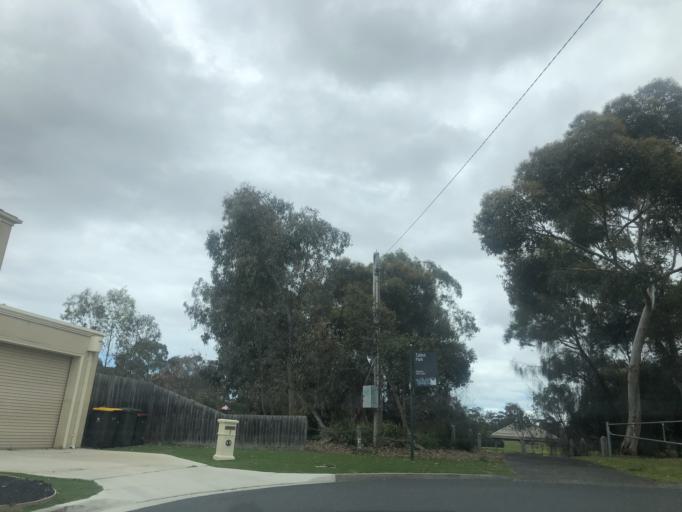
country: AU
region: Victoria
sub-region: Kingston
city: Clayton South
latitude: -37.9260
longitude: 145.1057
